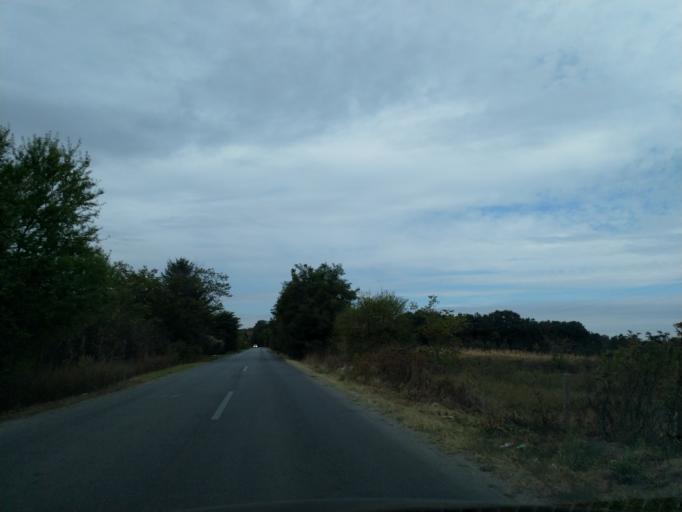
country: RS
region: Central Serbia
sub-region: Pomoravski Okrug
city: Jagodina
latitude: 44.0049
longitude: 21.2084
